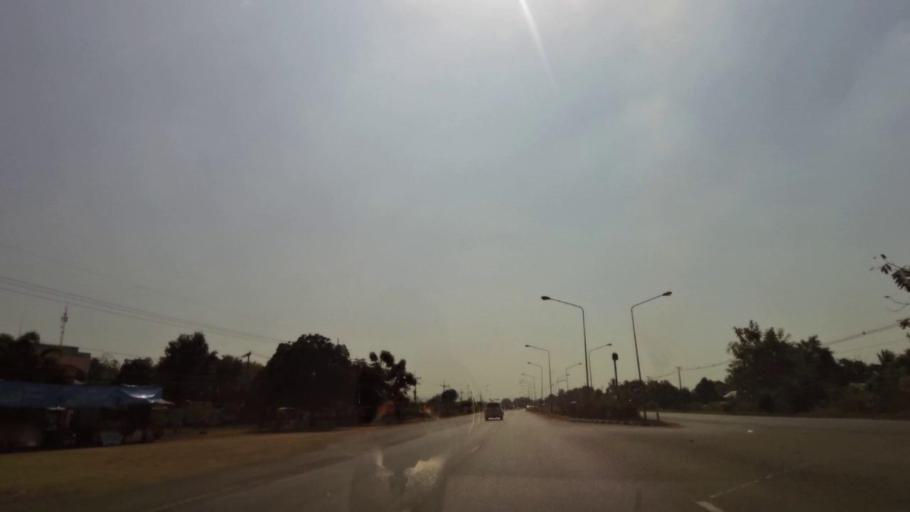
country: TH
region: Phichit
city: Wachira Barami
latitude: 16.3577
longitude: 100.1296
